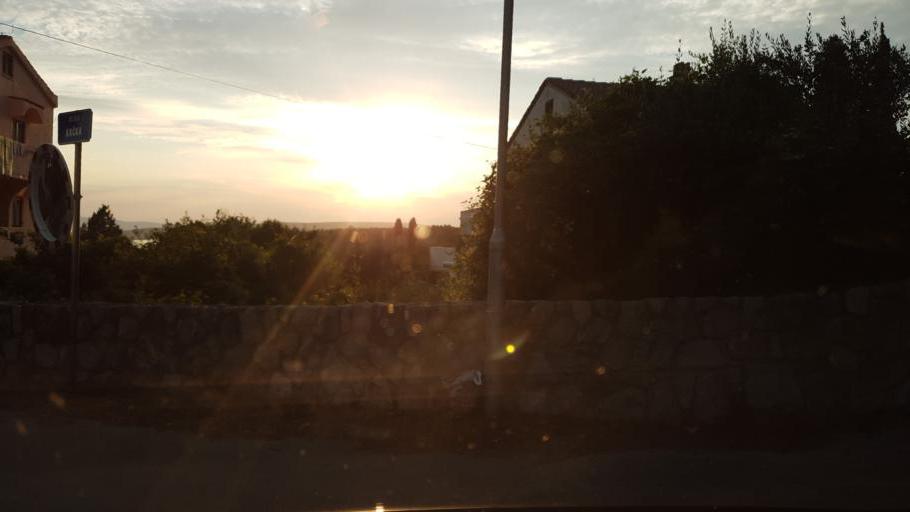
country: HR
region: Primorsko-Goranska
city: Punat
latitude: 45.0120
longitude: 14.6249
